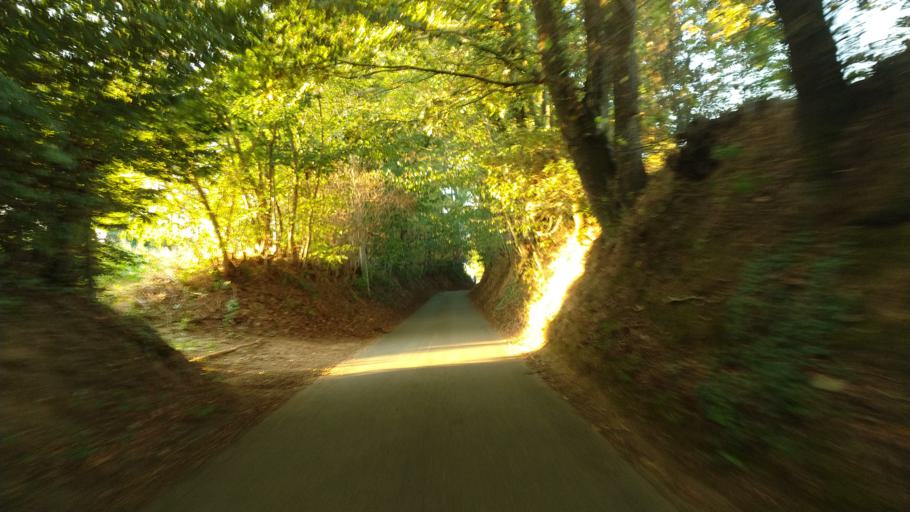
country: BE
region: Flanders
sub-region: Provincie Vlaams-Brabant
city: Holsbeek
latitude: 50.8852
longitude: 4.7832
